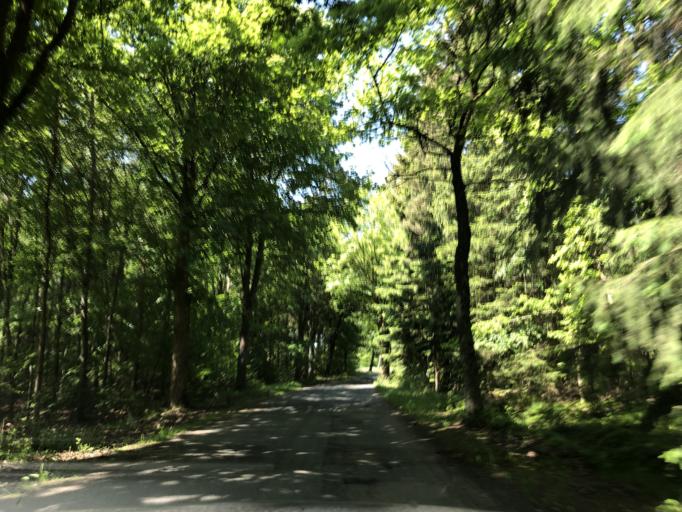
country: PL
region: West Pomeranian Voivodeship
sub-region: Powiat kolobrzeski
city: Goscino
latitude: 54.0257
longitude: 15.7369
